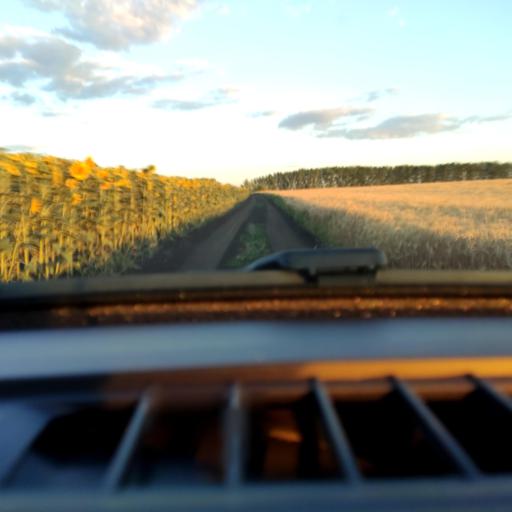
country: RU
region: Voronezj
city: Verkhnyaya Khava
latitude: 51.5827
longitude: 39.8723
